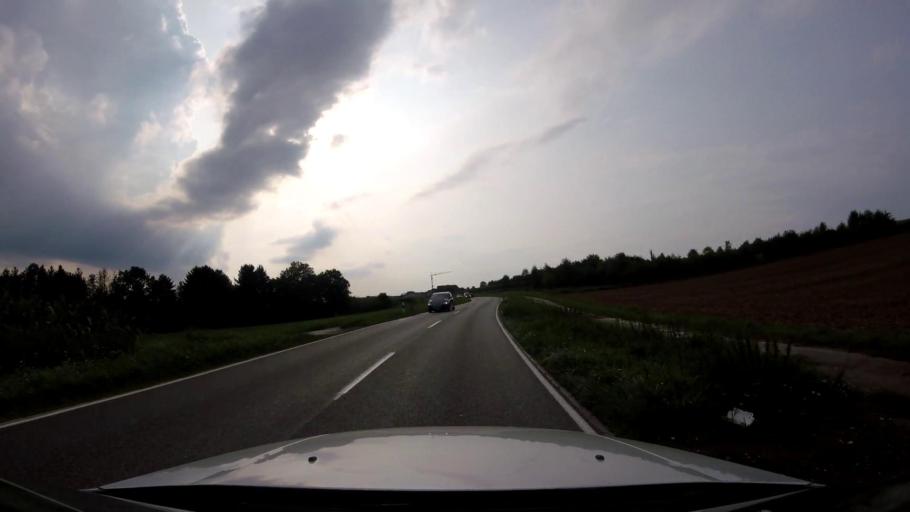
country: DE
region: Baden-Wuerttemberg
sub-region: Regierungsbezirk Stuttgart
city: Mutlangen
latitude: 48.8365
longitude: 9.7870
